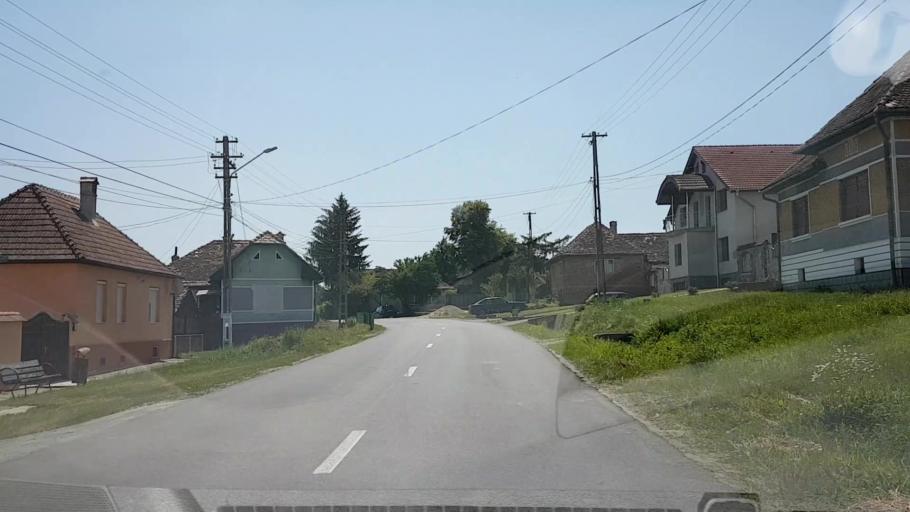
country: RO
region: Sibiu
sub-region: Comuna Merghindeal
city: Merghindeal
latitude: 45.9637
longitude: 24.7337
